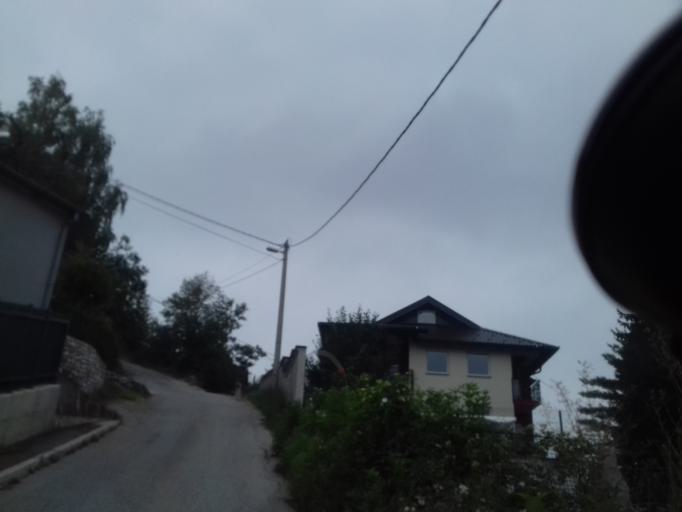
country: BA
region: Federation of Bosnia and Herzegovina
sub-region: Kanton Sarajevo
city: Sarajevo
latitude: 43.8409
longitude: 18.3528
